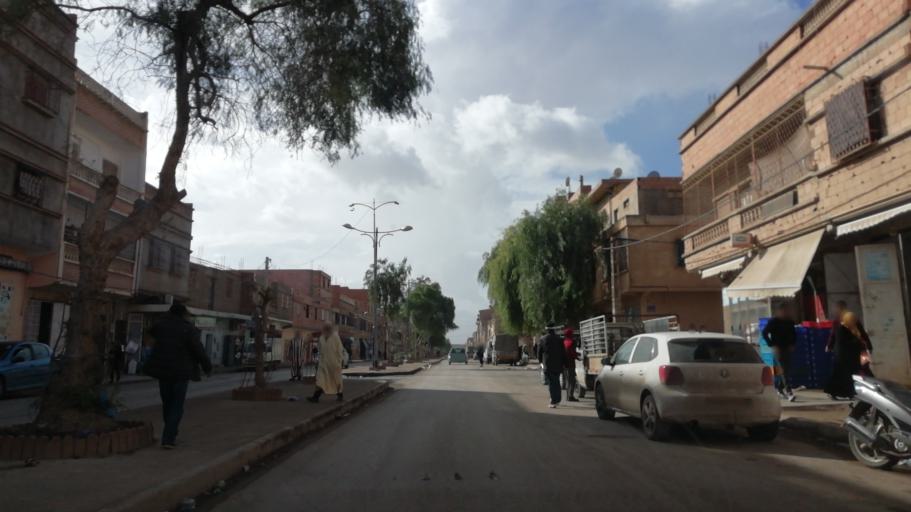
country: DZ
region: Oran
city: Es Senia
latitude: 35.6421
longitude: -0.5736
